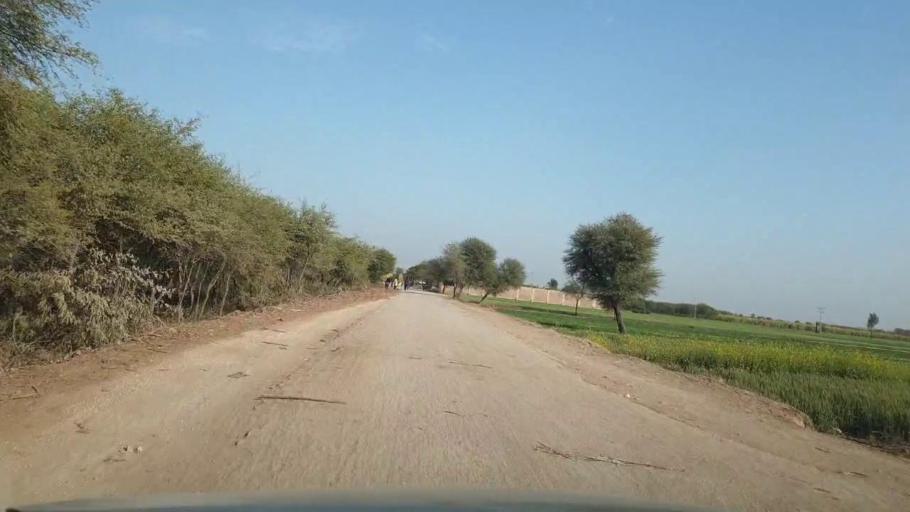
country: PK
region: Sindh
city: Tando Allahyar
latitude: 25.5937
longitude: 68.6752
